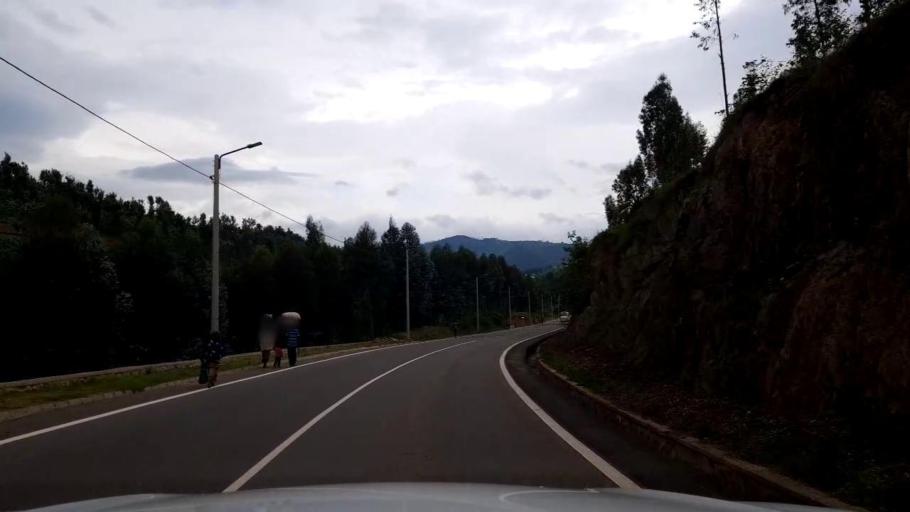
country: RW
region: Western Province
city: Kibuye
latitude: -2.0214
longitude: 29.3885
